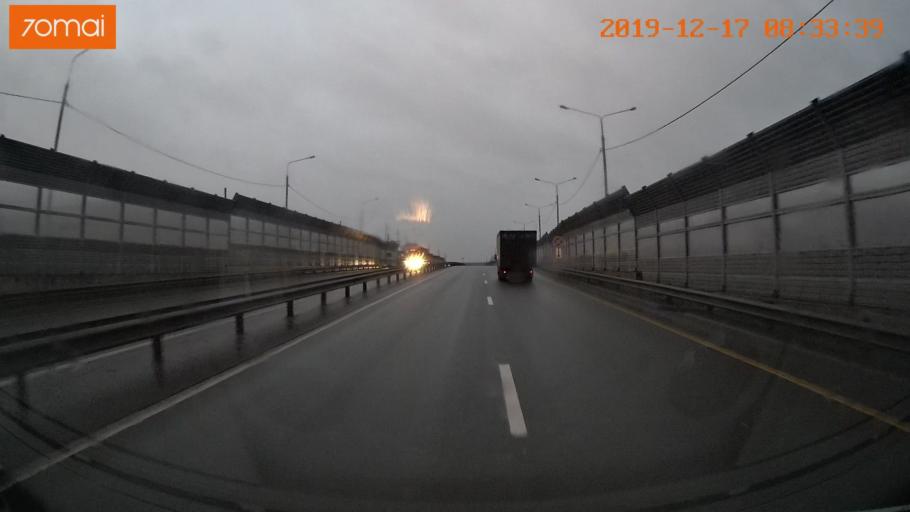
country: RU
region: Vladimir
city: Lakinsk
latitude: 56.0089
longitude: 39.9347
